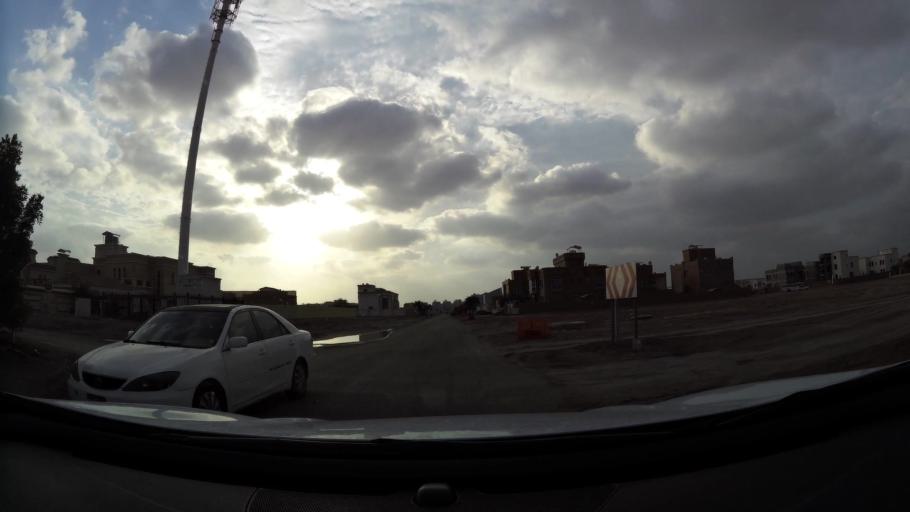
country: AE
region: Abu Dhabi
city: Abu Dhabi
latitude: 24.3522
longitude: 54.5586
